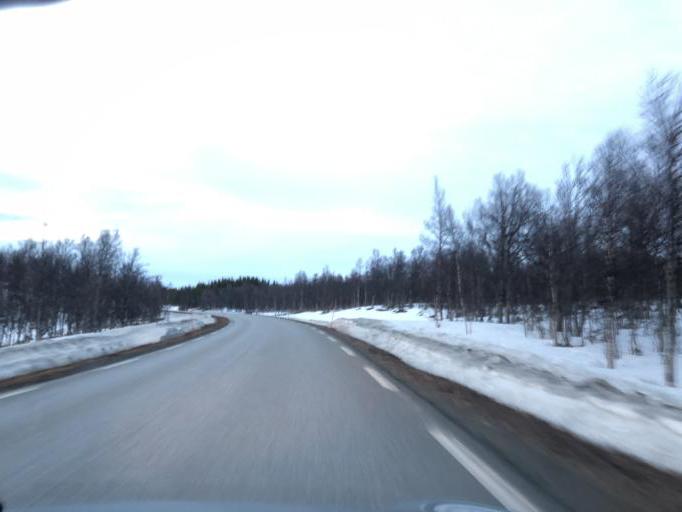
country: NO
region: Sor-Trondelag
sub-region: Tydal
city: Aas
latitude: 62.7150
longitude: 11.8167
